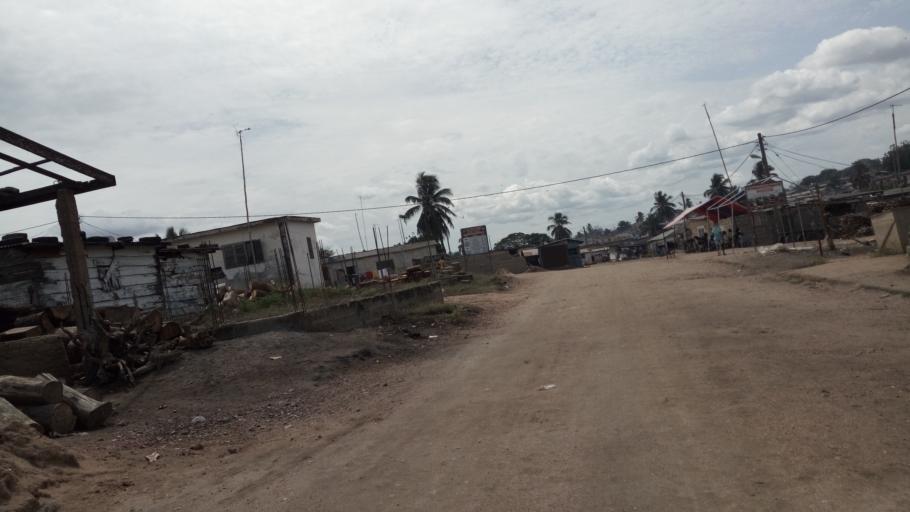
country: GH
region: Central
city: Winneba
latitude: 5.3480
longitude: -0.6160
